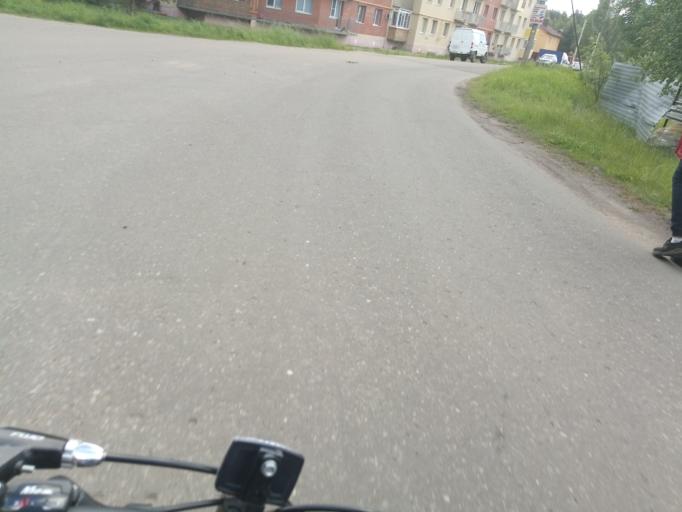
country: RU
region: Jaroslavl
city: Yaroslavl
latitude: 57.6564
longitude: 39.9801
